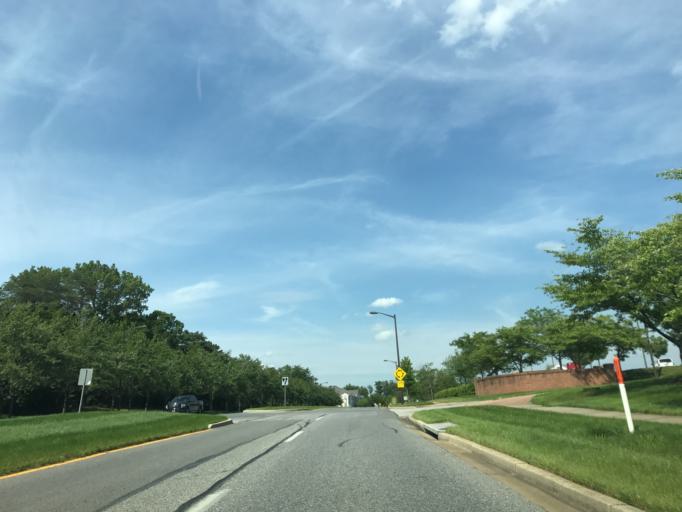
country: US
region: Maryland
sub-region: Anne Arundel County
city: Odenton
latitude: 39.0653
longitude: -76.7217
